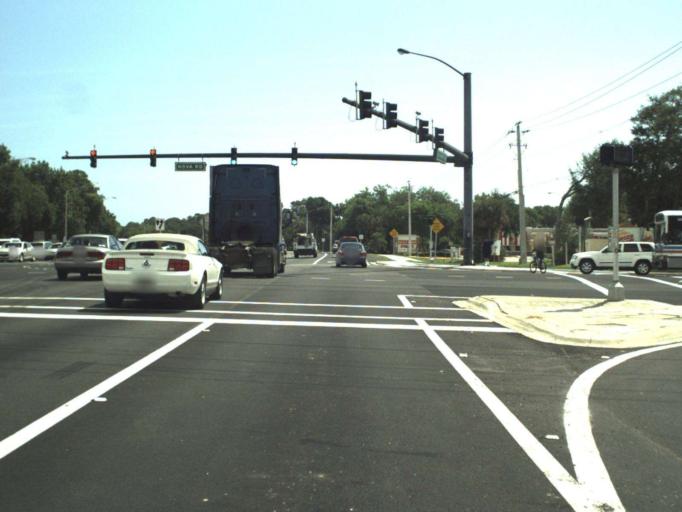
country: US
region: Florida
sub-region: Volusia County
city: Port Orange
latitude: 29.1273
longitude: -81.0054
